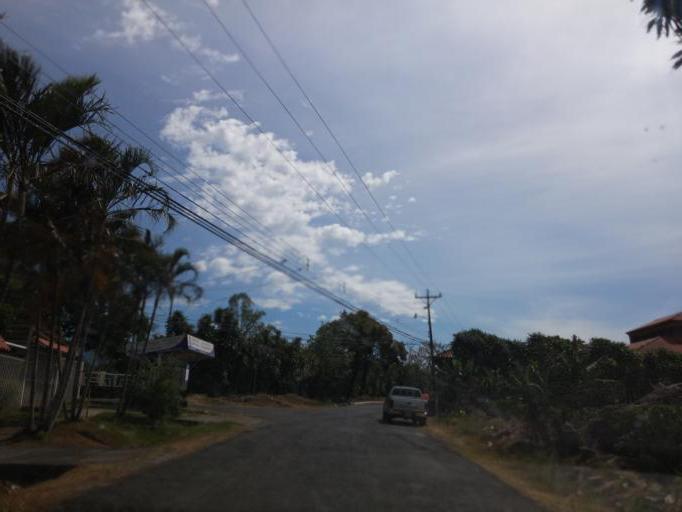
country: CR
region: Alajuela
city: Sabanilla
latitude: 10.0441
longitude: -84.2309
